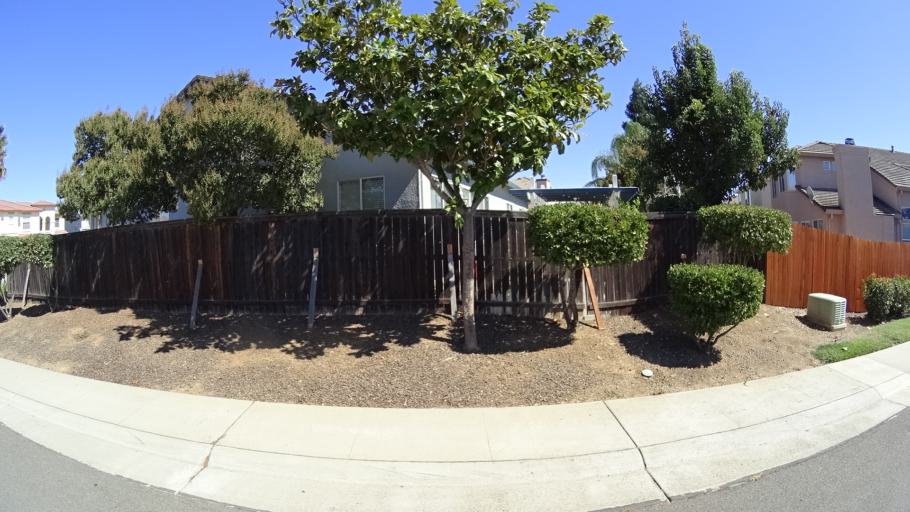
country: US
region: California
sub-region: Sacramento County
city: Elk Grove
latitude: 38.4146
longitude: -121.3481
